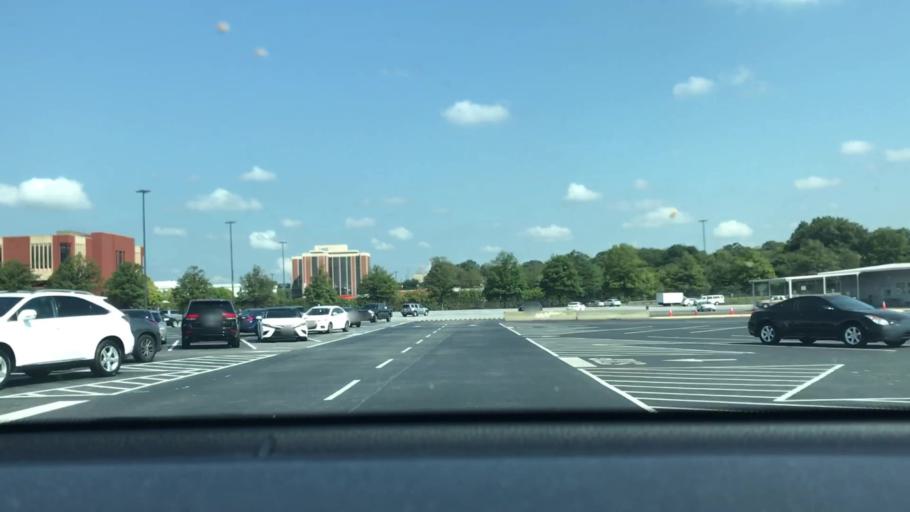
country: US
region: Georgia
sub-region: Fulton County
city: Hapeville
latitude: 33.6559
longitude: -84.4207
